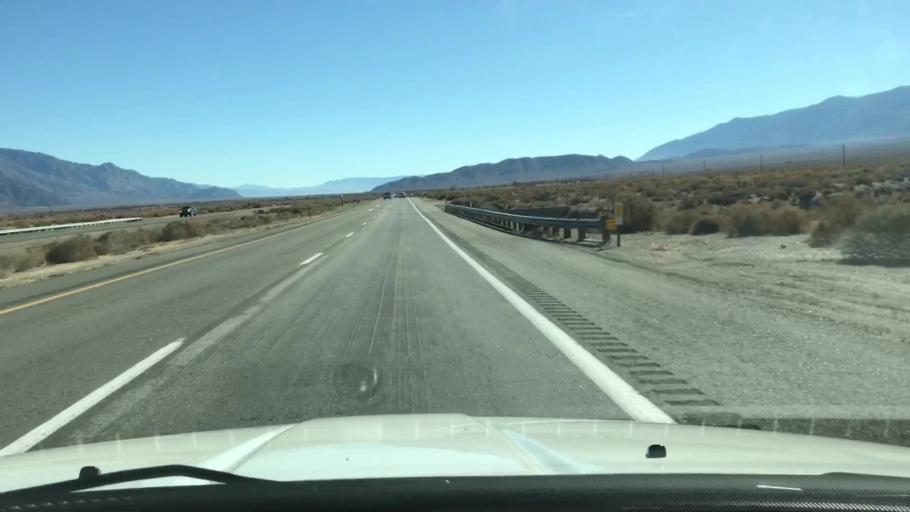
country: US
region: California
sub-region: Inyo County
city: Lone Pine
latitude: 36.7758
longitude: -118.1809
